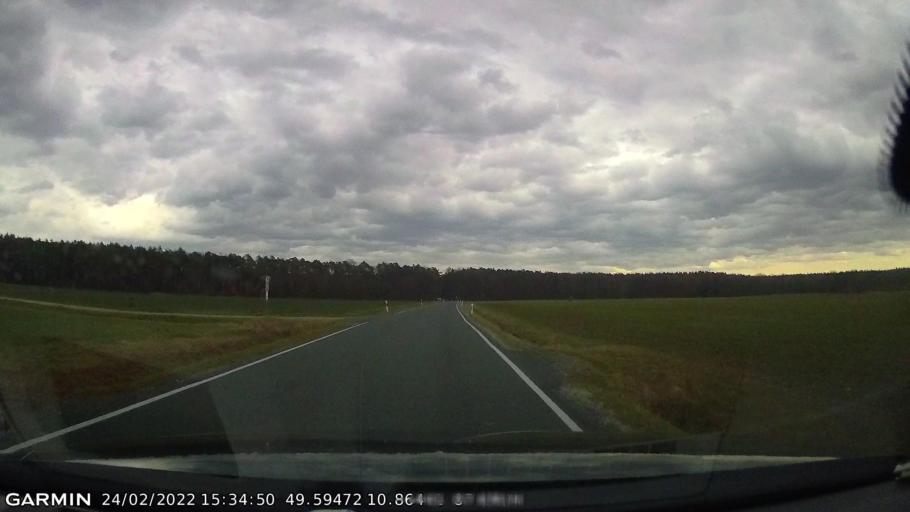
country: DE
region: Bavaria
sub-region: Regierungsbezirk Mittelfranken
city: Herzogenaurach
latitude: 49.5947
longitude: 10.8646
